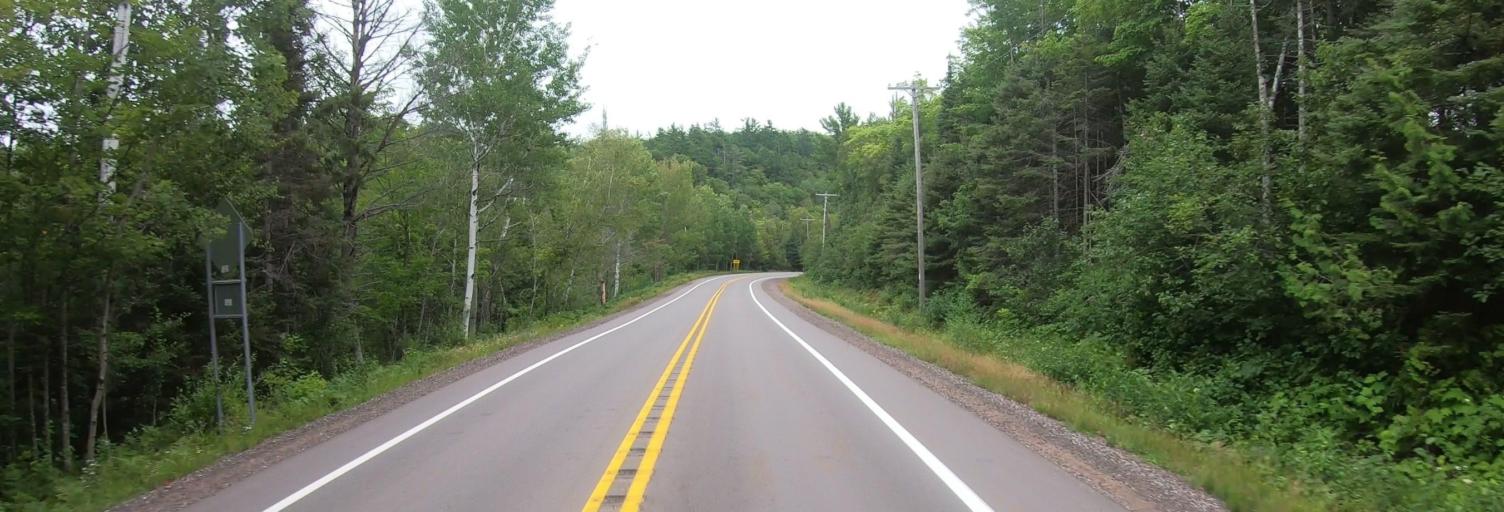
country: US
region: Michigan
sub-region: Keweenaw County
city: Eagle River
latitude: 47.3958
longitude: -88.2801
